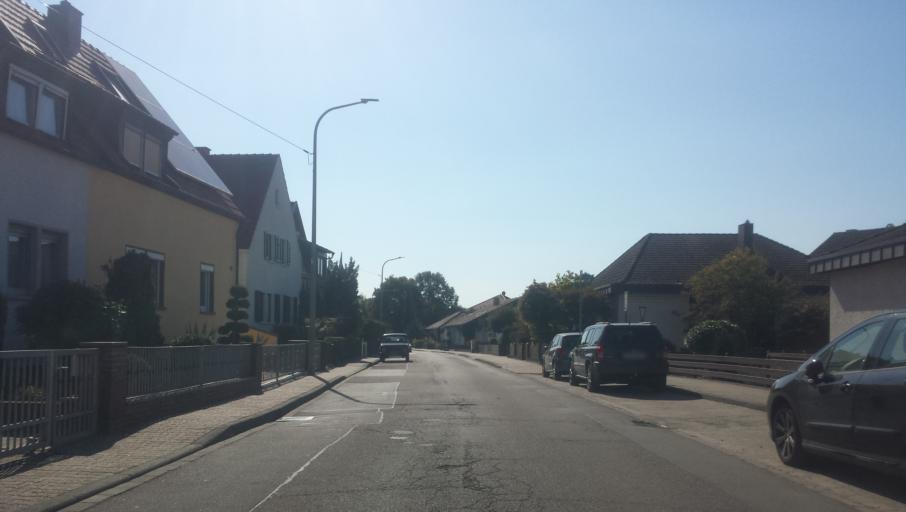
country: DE
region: Rheinland-Pfalz
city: Neuhofen
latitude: 49.4250
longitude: 8.4229
